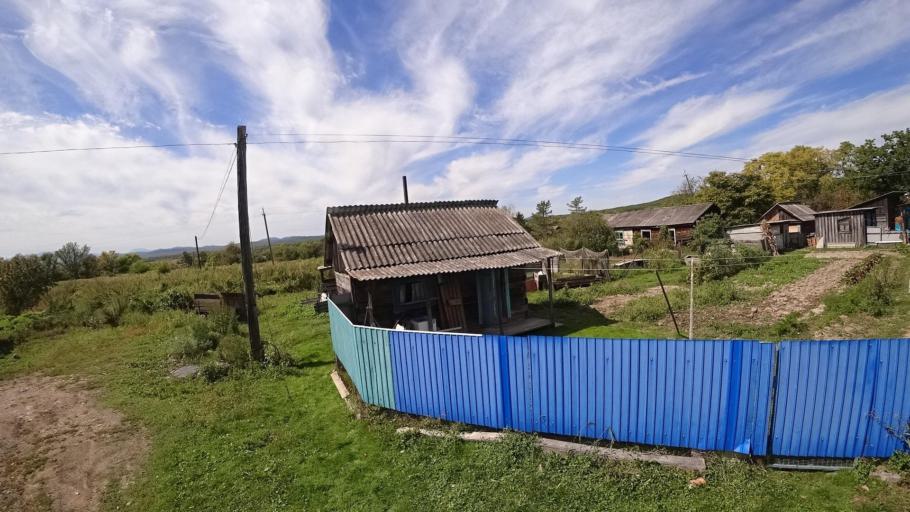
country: RU
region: Primorskiy
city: Yakovlevka
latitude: 44.6457
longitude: 133.5910
